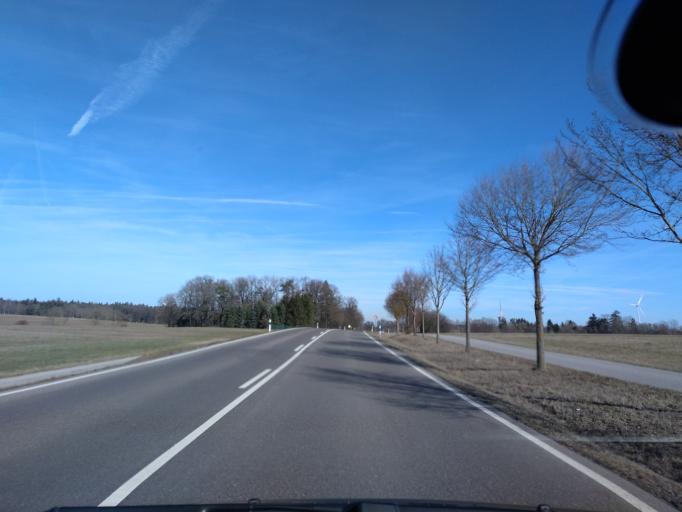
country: DE
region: Baden-Wuerttemberg
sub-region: Regierungsbezirk Stuttgart
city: Mainhardt
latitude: 49.0839
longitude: 9.5983
